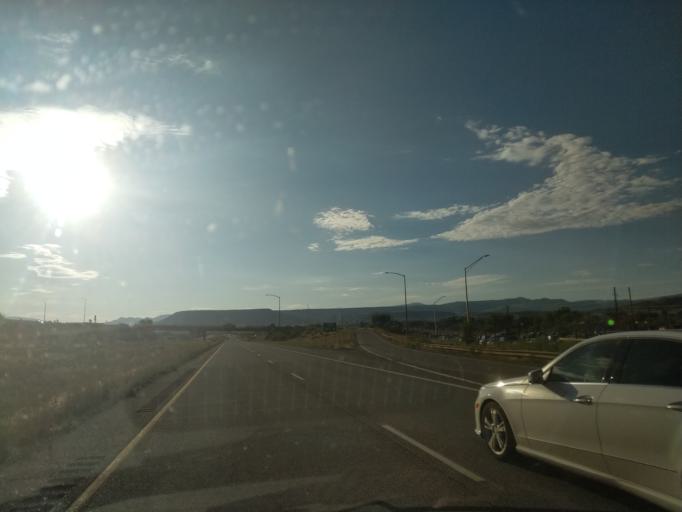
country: US
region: Colorado
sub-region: Garfield County
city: Silt
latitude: 39.5451
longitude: -107.6574
